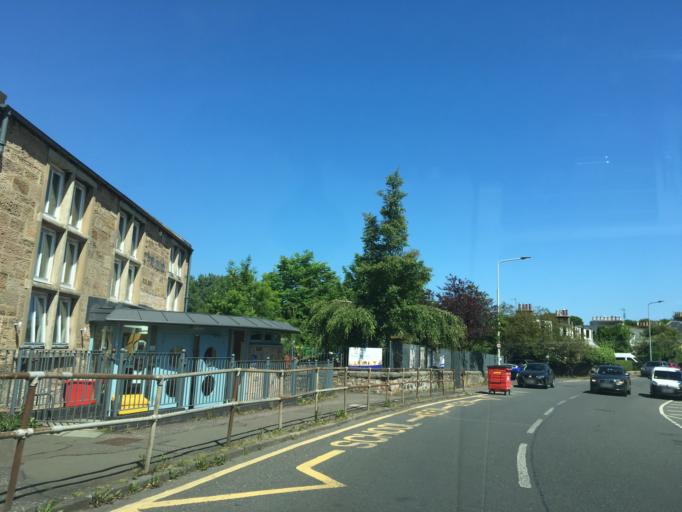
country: GB
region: Scotland
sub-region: Fife
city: Aberdour
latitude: 55.9750
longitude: -3.3018
